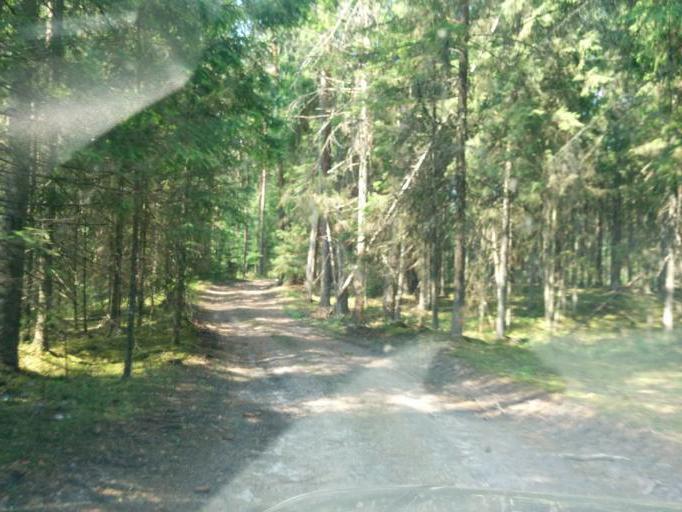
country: LV
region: Ikskile
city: Ikskile
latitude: 56.7450
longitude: 24.4972
